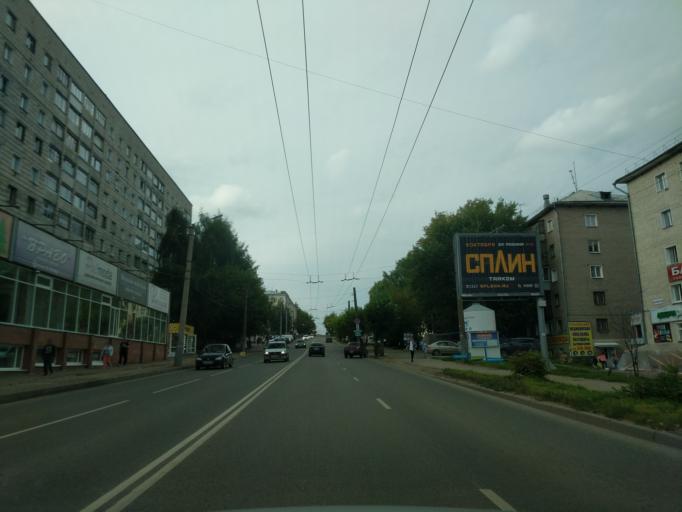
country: RU
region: Kirov
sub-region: Kirovo-Chepetskiy Rayon
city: Kirov
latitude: 58.5897
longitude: 49.6693
